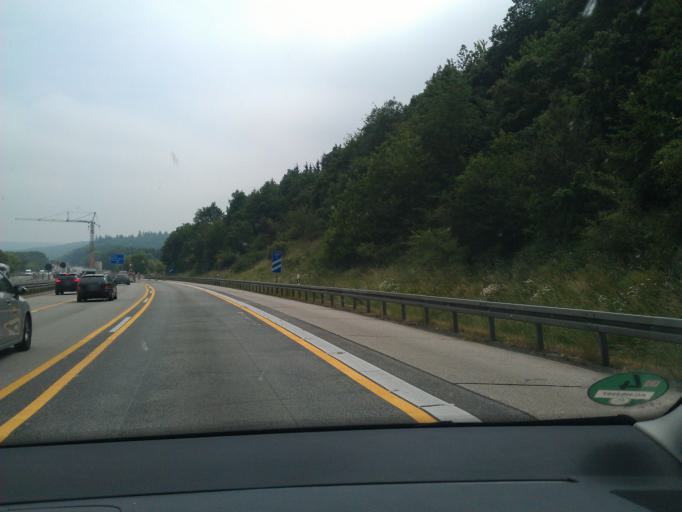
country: DE
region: Hesse
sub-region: Regierungsbezirk Darmstadt
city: Idstein
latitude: 50.2161
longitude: 8.2499
